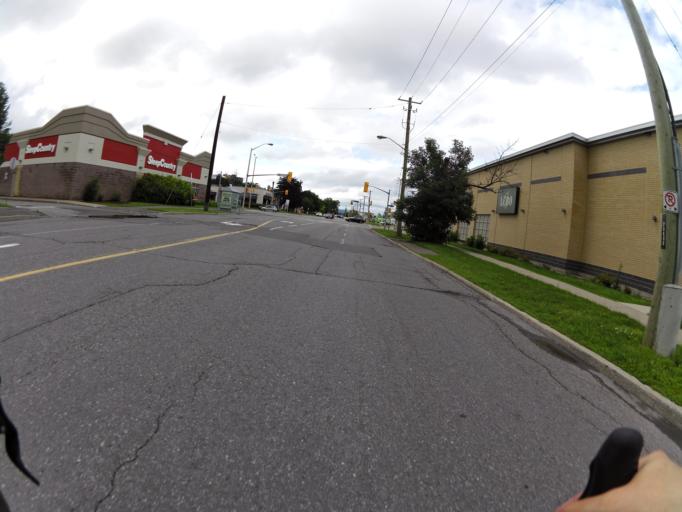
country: CA
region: Ontario
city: Bells Corners
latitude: 45.3695
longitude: -75.7702
